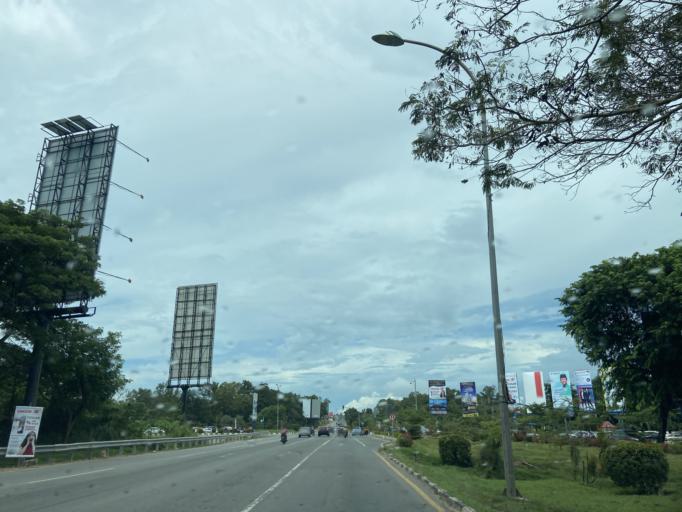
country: SG
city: Singapore
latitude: 1.1028
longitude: 104.0378
